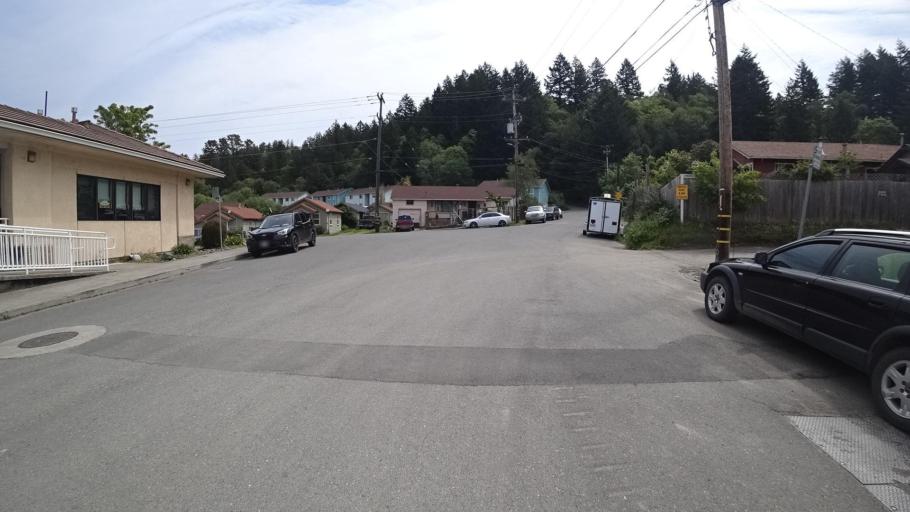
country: US
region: California
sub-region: Humboldt County
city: Redway
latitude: 40.0978
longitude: -123.7942
